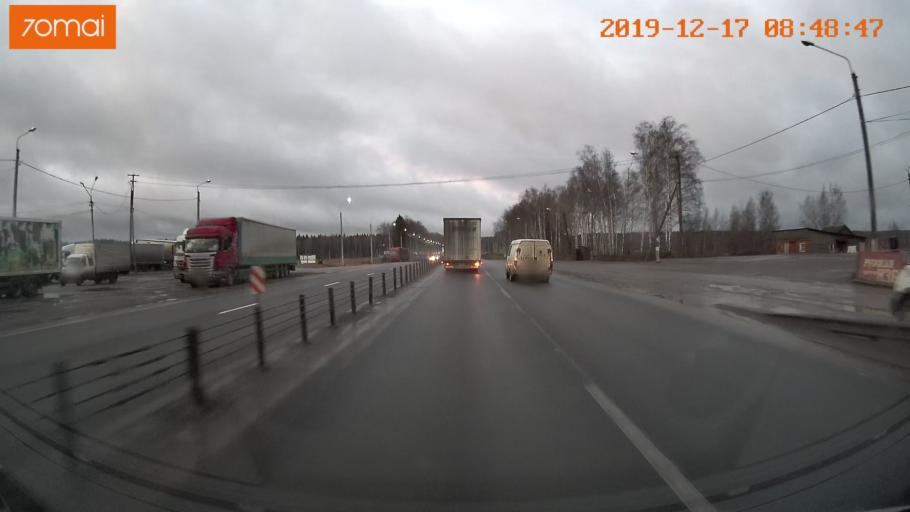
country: RU
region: Vladimir
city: Kosterevo
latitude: 55.9554
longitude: 39.6085
